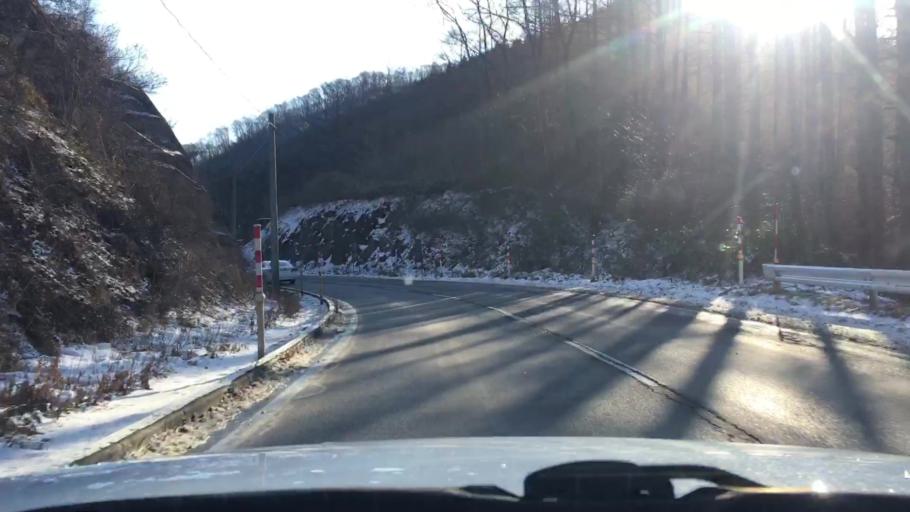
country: JP
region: Iwate
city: Morioka-shi
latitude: 39.6657
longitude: 141.3048
